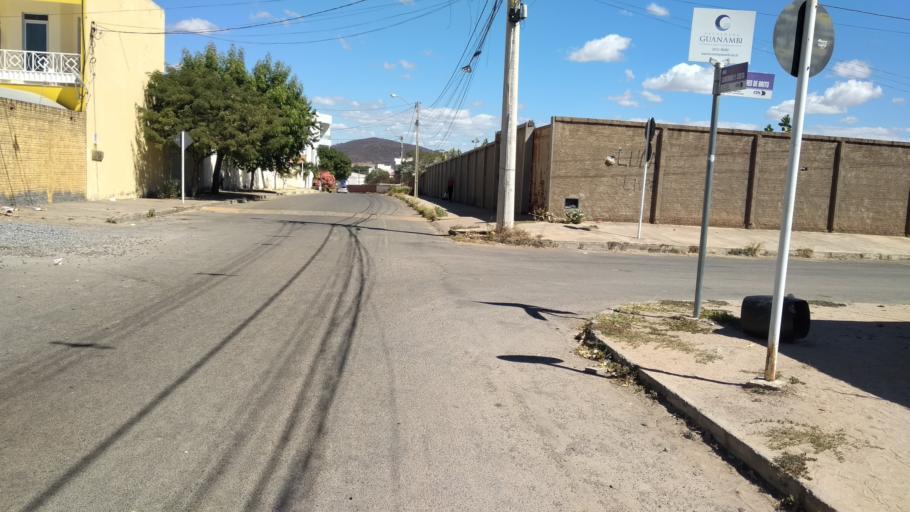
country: BR
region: Bahia
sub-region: Guanambi
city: Guanambi
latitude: -14.2297
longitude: -42.7767
